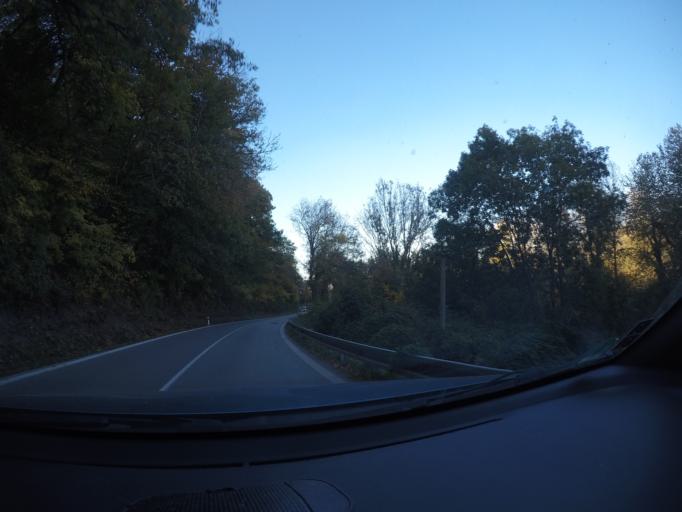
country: SK
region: Trenciansky
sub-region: Okres Trencin
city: Trencin
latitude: 48.9098
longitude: 18.0747
